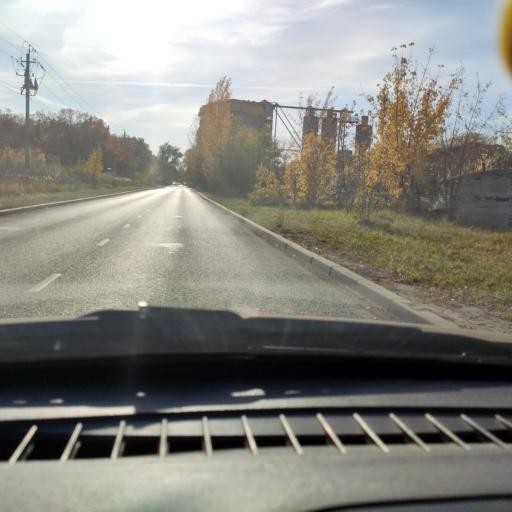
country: RU
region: Samara
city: Tol'yatti
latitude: 53.5177
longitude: 49.3151
